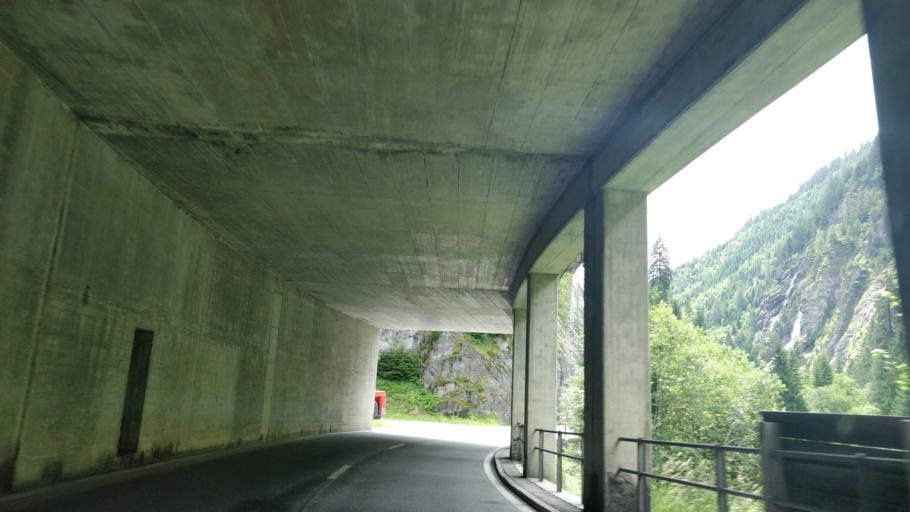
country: CH
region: Grisons
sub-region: Hinterrhein District
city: Hinterrhein
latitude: 46.6486
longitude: 9.1867
